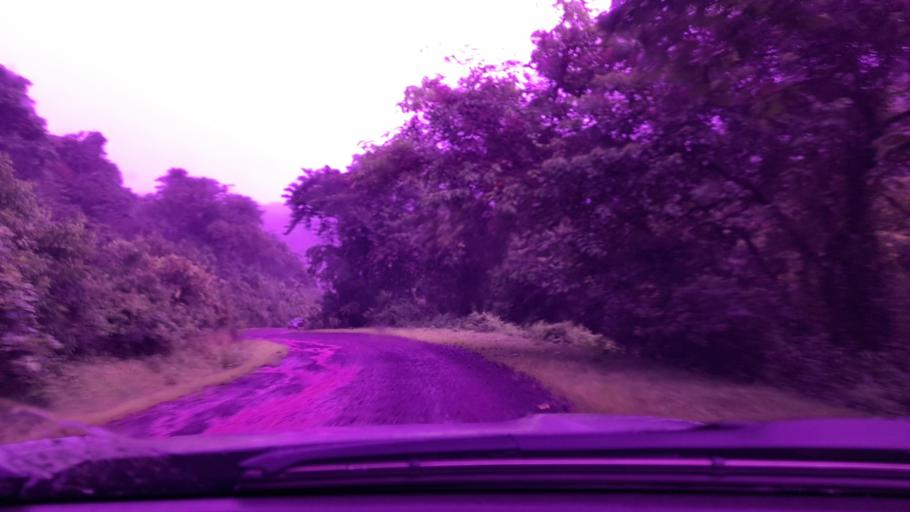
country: ET
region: Oromiya
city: Metu
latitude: 8.4781
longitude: 35.6408
